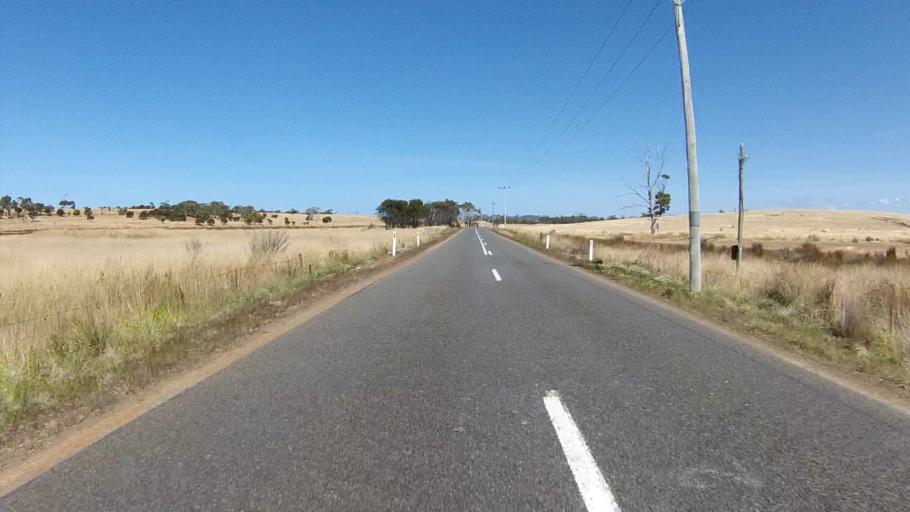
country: AU
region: Tasmania
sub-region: Sorell
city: Sorell
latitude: -42.2744
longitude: 148.0042
